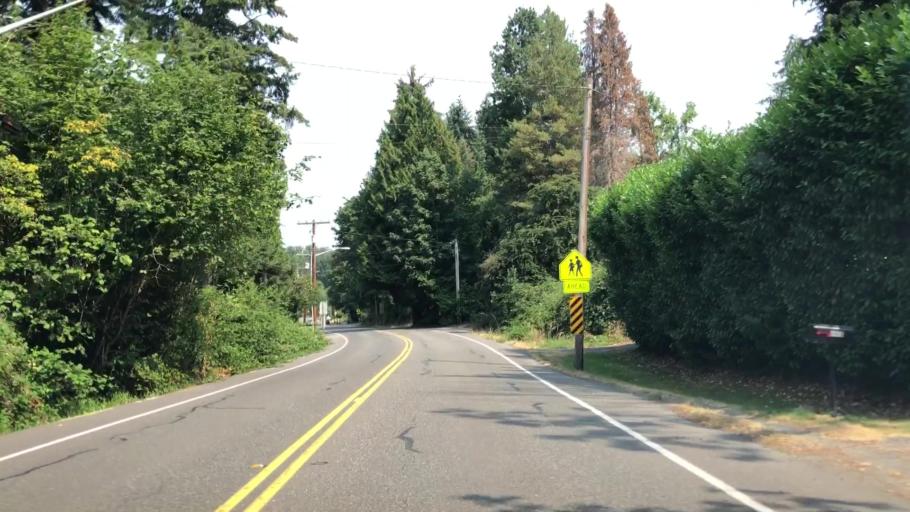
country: US
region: Washington
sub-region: Snohomish County
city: Brier
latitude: 47.7747
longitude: -122.2559
